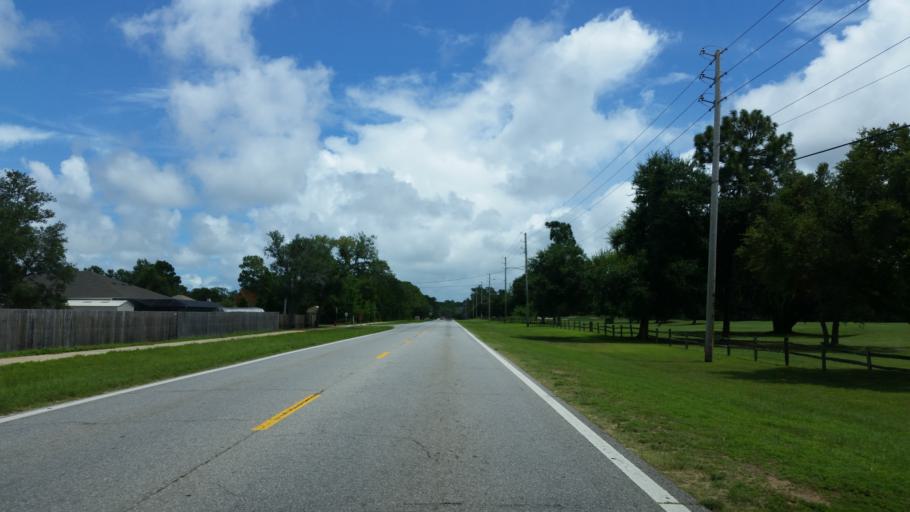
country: US
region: Florida
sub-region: Santa Rosa County
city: Holley
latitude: 30.4424
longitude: -86.9232
